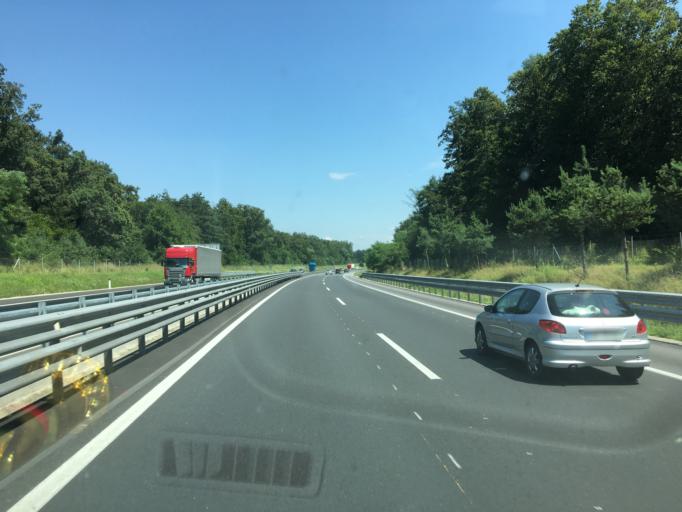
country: SI
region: Hoce-Slivnica
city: Rogoza
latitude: 46.5146
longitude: 15.6729
